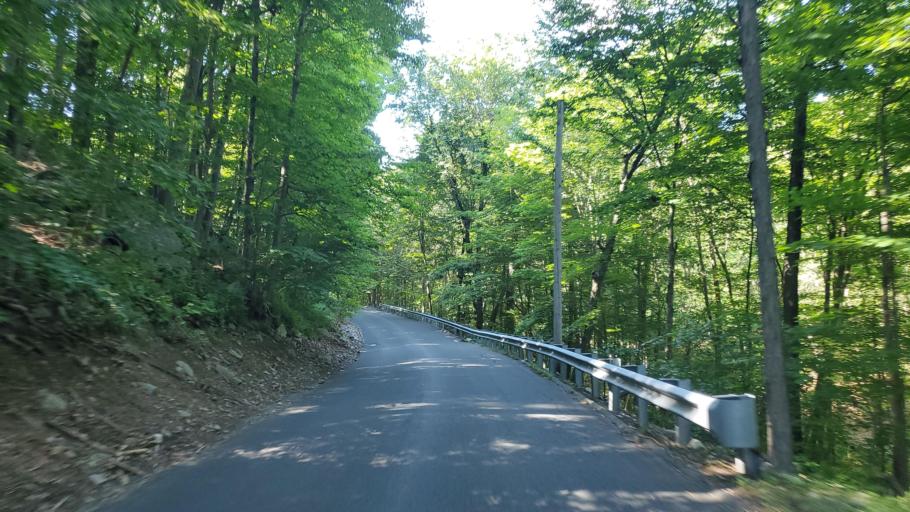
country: US
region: Connecticut
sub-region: Fairfield County
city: Newtown
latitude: 41.3381
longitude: -73.2917
